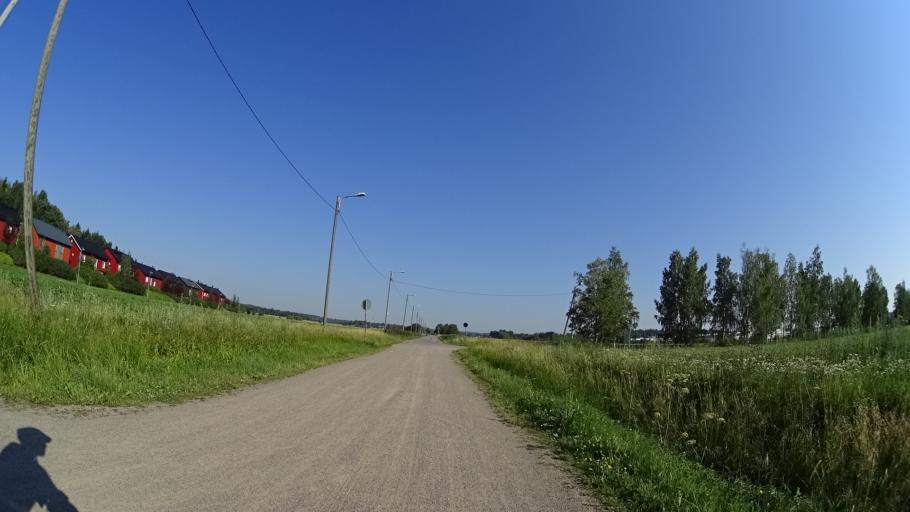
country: FI
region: Uusimaa
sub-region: Helsinki
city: Vantaa
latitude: 60.2638
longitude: 24.9615
